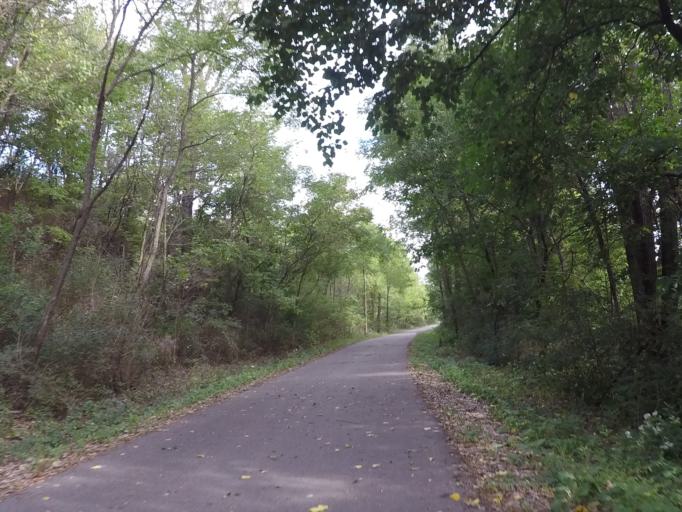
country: US
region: Wisconsin
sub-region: Sauk County
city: Prairie du Sac
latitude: 43.3024
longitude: -89.7310
